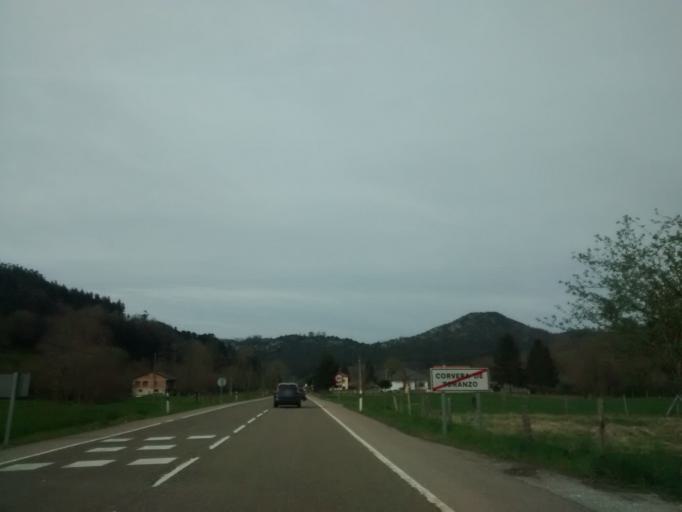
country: ES
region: Cantabria
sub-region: Provincia de Cantabria
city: Corvera
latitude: 43.2692
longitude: -3.9471
